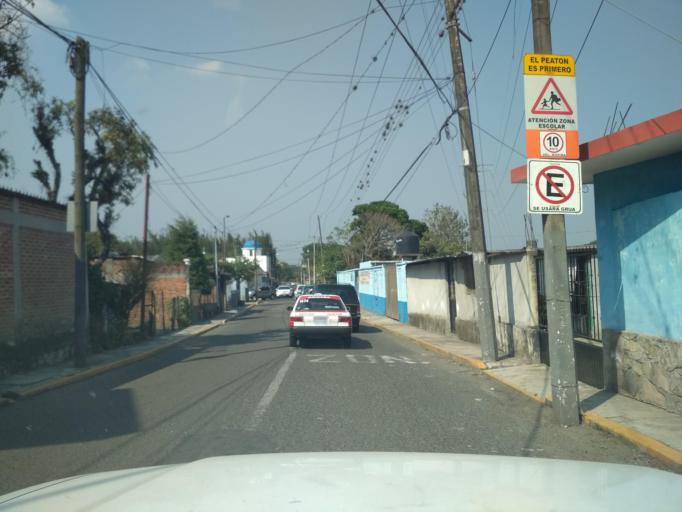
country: MX
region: Veracruz
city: Jalapilla
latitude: 18.8386
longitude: -97.0810
